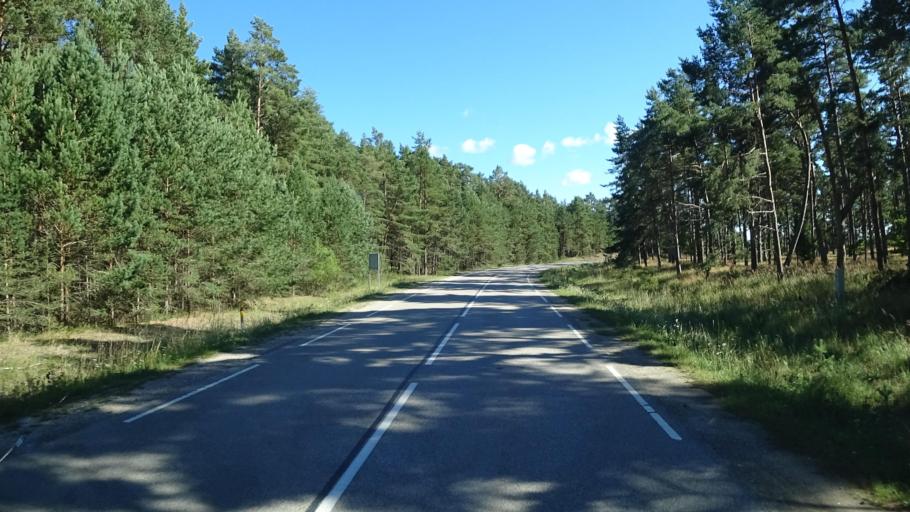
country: LV
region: Rojas
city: Roja
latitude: 57.7537
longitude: 22.5954
